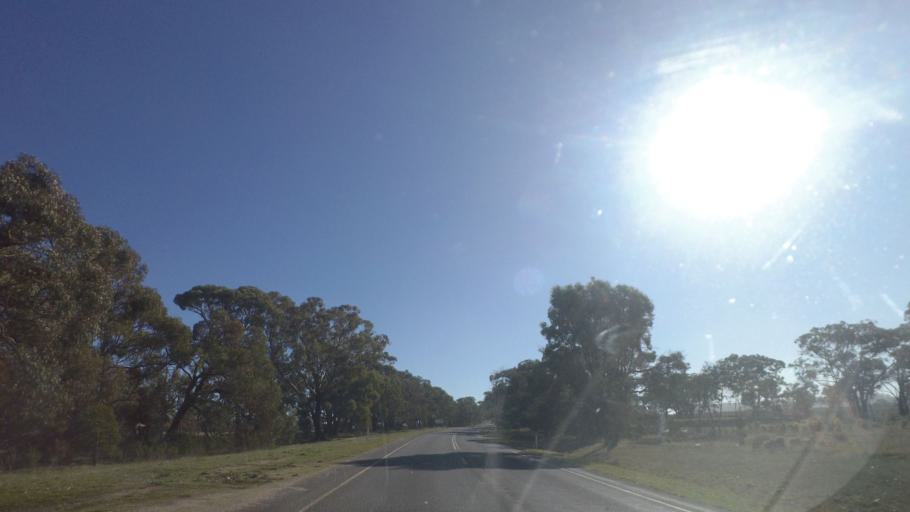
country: AU
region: Victoria
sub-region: Mount Alexander
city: Castlemaine
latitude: -37.0636
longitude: 144.2982
